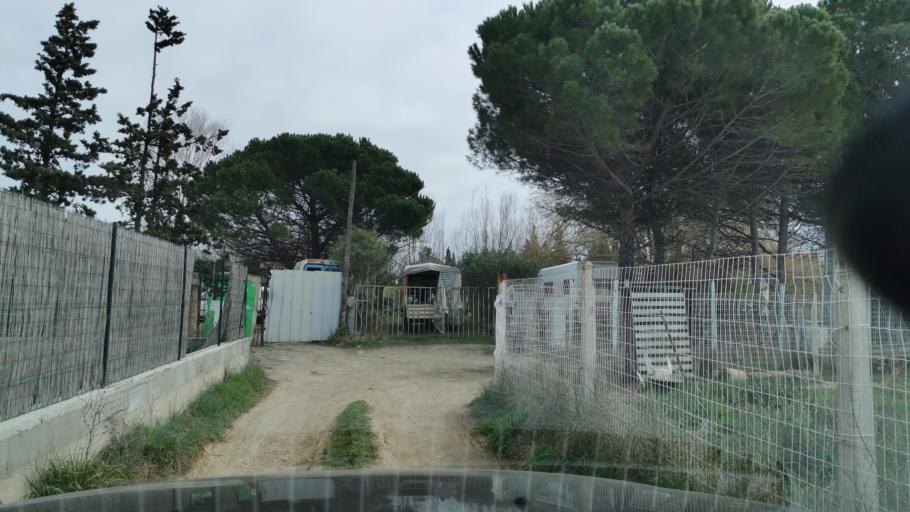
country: FR
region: Languedoc-Roussillon
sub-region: Departement de l'Aude
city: Narbonne
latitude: 43.1960
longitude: 2.9998
